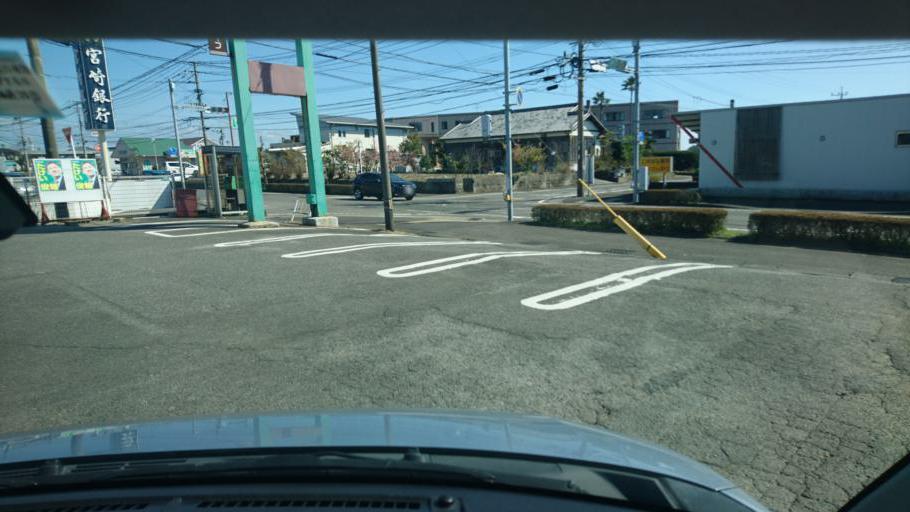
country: JP
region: Miyazaki
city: Miyazaki-shi
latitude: 31.8286
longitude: 131.4370
